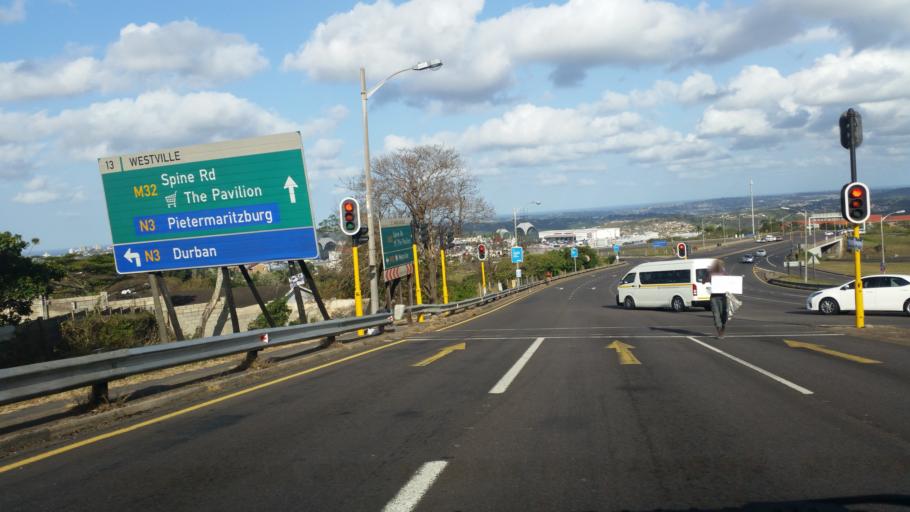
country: ZA
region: KwaZulu-Natal
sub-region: eThekwini Metropolitan Municipality
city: Berea
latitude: -29.8463
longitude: 30.9298
